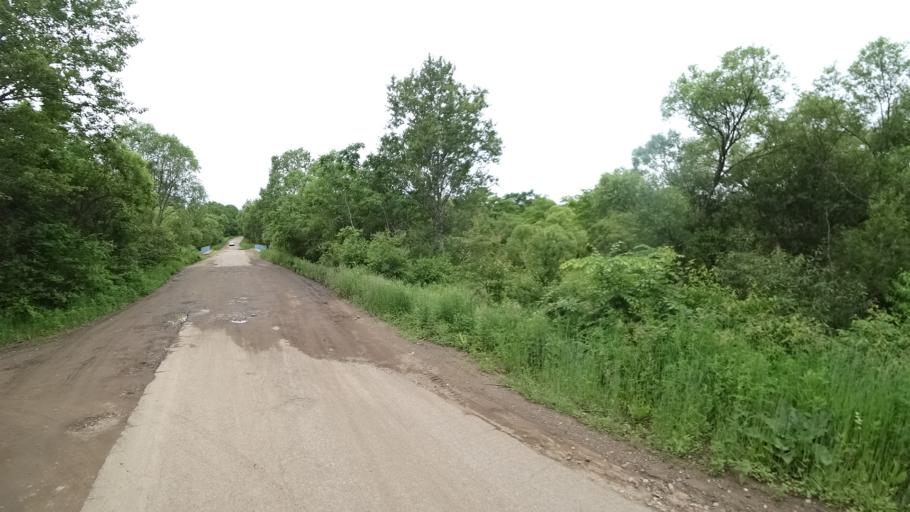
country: RU
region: Primorskiy
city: Novosysoyevka
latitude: 44.2046
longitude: 133.3260
